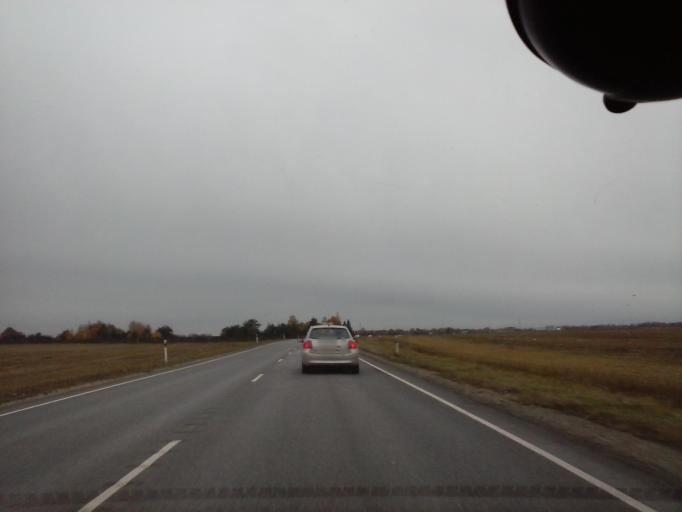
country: EE
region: Jogevamaa
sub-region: Poltsamaa linn
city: Poltsamaa
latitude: 58.6494
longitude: 26.0318
